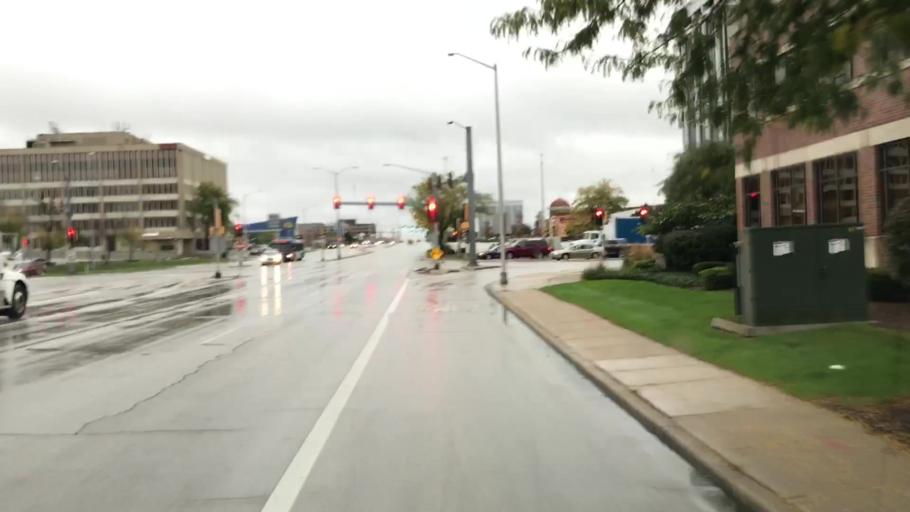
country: US
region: Wisconsin
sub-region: Waukesha County
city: Elm Grove
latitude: 43.0594
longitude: -88.0475
